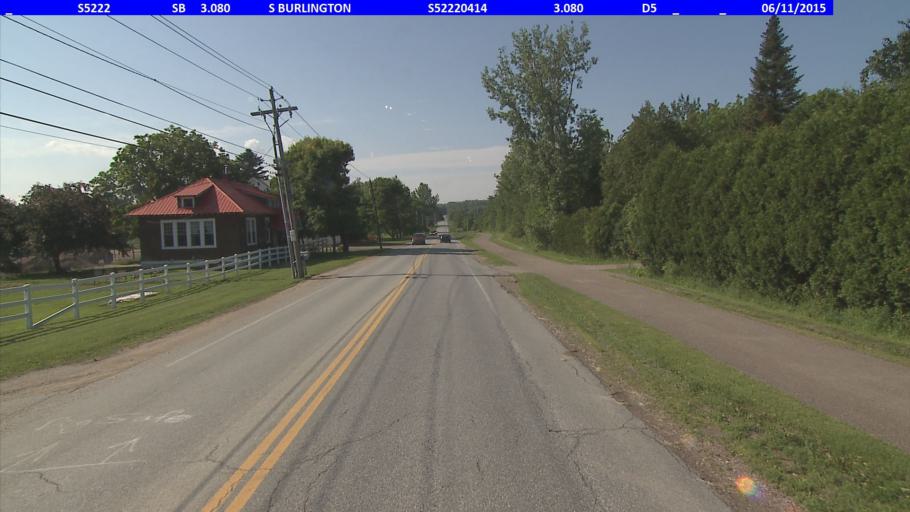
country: US
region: Vermont
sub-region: Chittenden County
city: South Burlington
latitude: 44.4607
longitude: -73.1904
